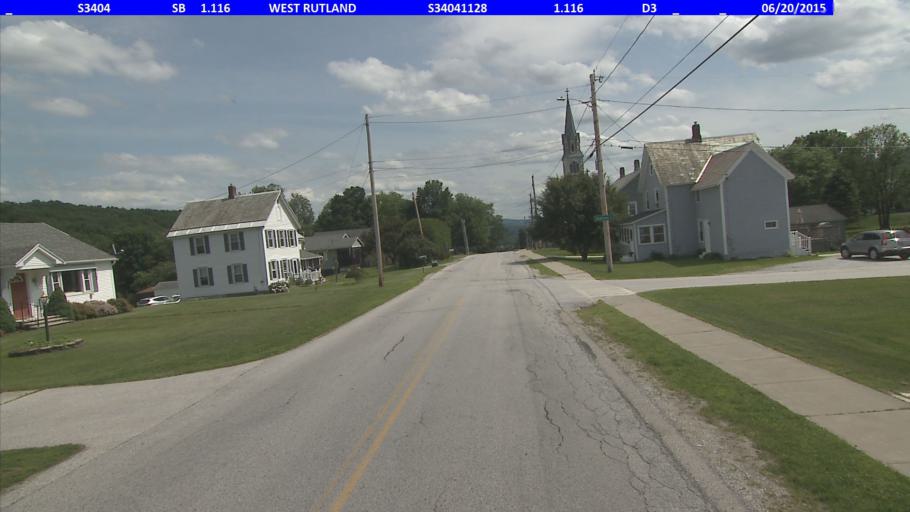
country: US
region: Vermont
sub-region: Rutland County
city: West Rutland
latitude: 43.6075
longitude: -73.0489
